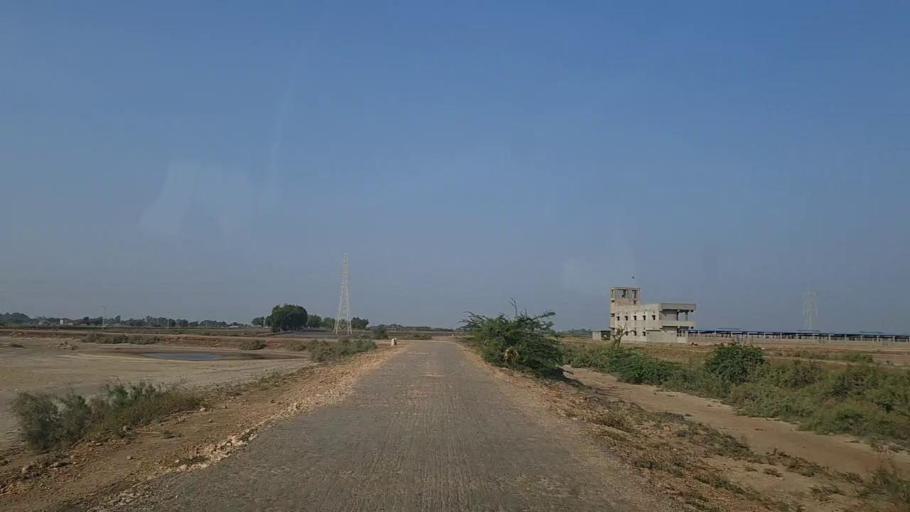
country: PK
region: Sindh
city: Mirpur Sakro
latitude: 24.5617
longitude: 67.6710
